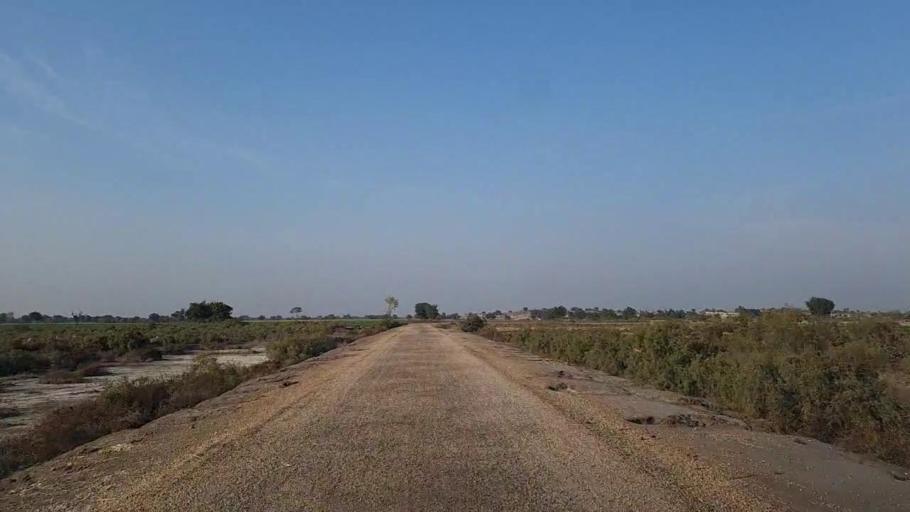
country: PK
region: Sindh
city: Jam Sahib
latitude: 26.3752
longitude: 68.5273
